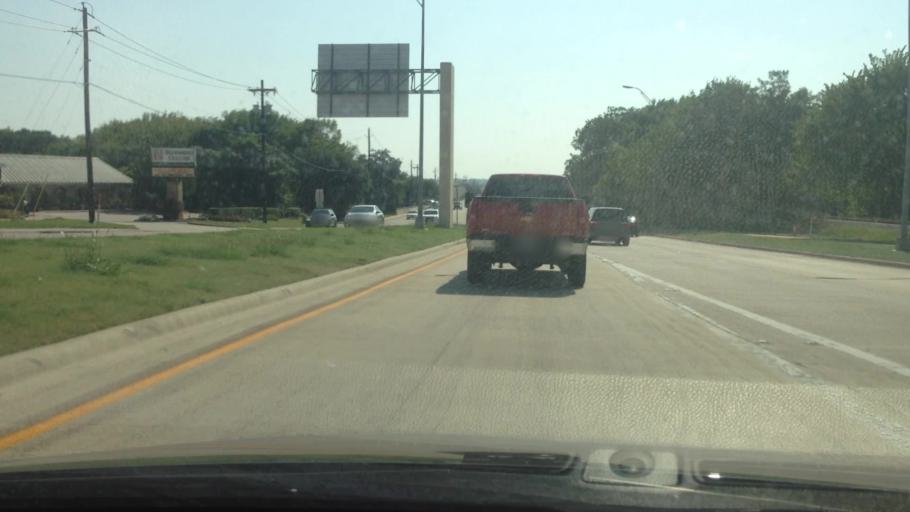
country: US
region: Texas
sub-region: Tarrant County
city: Grapevine
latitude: 32.9289
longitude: -97.1018
